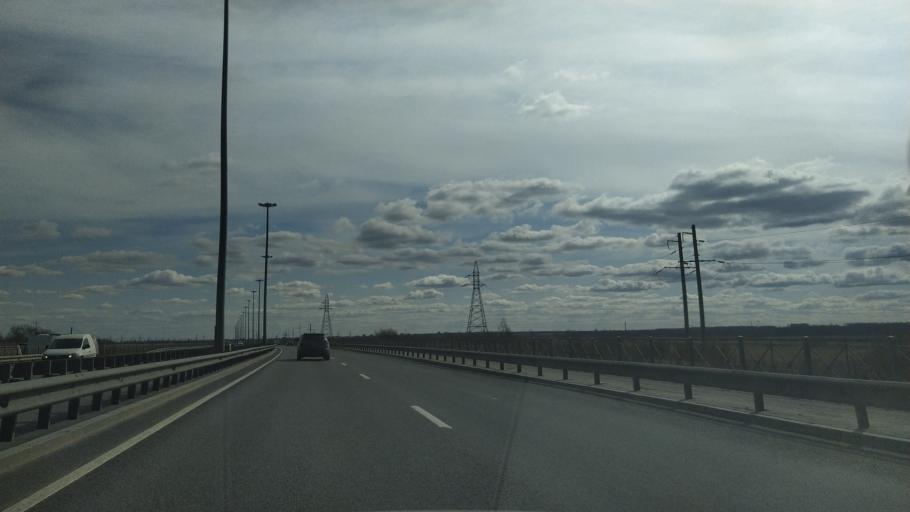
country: RU
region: St.-Petersburg
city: Shushary
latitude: 59.7860
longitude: 30.3942
